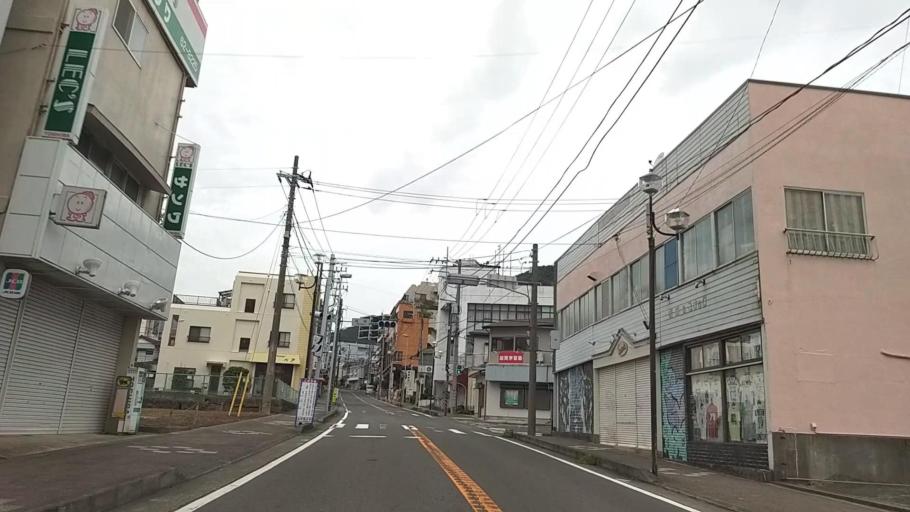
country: JP
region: Kanagawa
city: Yugawara
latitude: 35.1460
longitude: 139.1061
